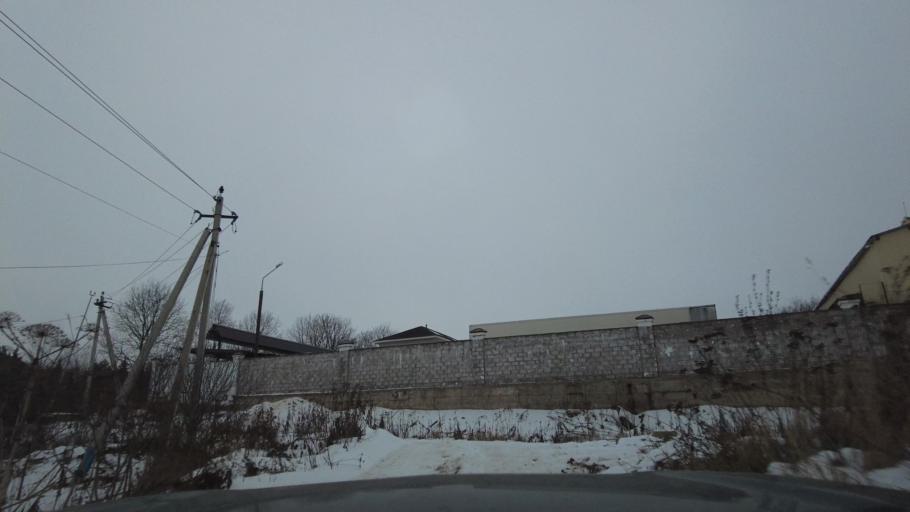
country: RU
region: Moskovskaya
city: Novopodrezkovo
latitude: 55.9906
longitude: 37.3929
